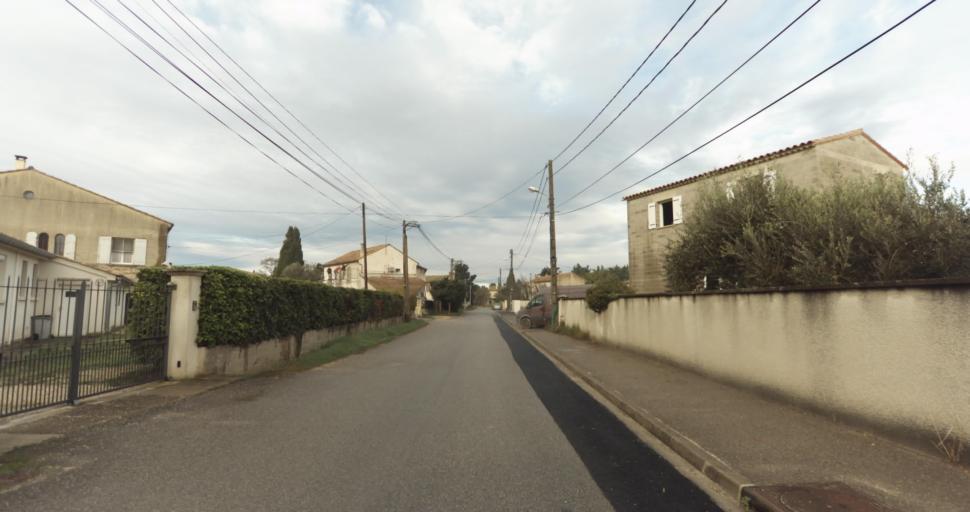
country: FR
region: Provence-Alpes-Cote d'Azur
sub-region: Departement des Bouches-du-Rhone
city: Rognonas
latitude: 43.8990
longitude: 4.7986
